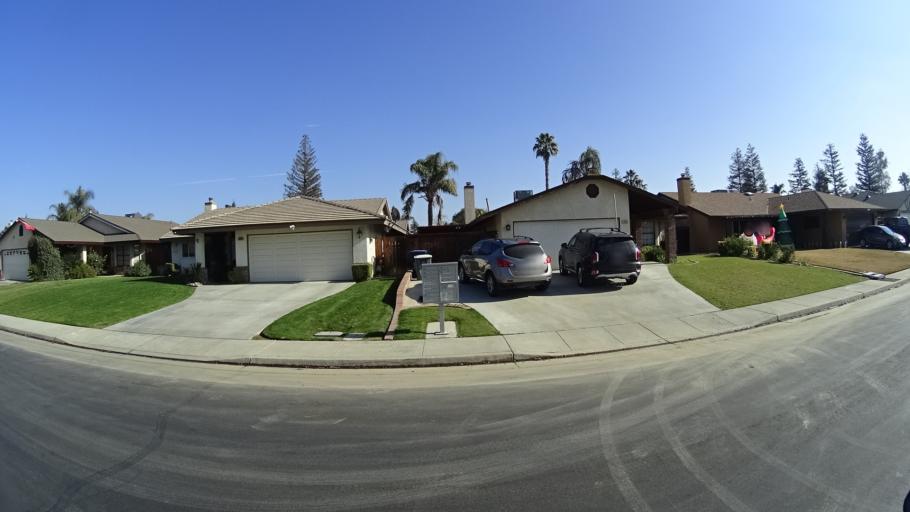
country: US
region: California
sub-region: Kern County
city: Greenacres
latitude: 35.3218
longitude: -119.1240
